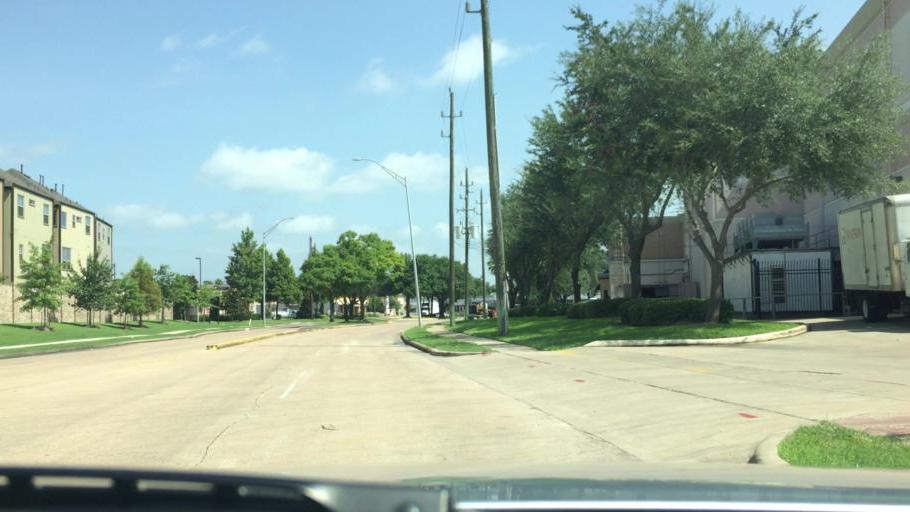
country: US
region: Texas
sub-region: Harris County
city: Bunker Hill Village
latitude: 29.7344
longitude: -95.5954
